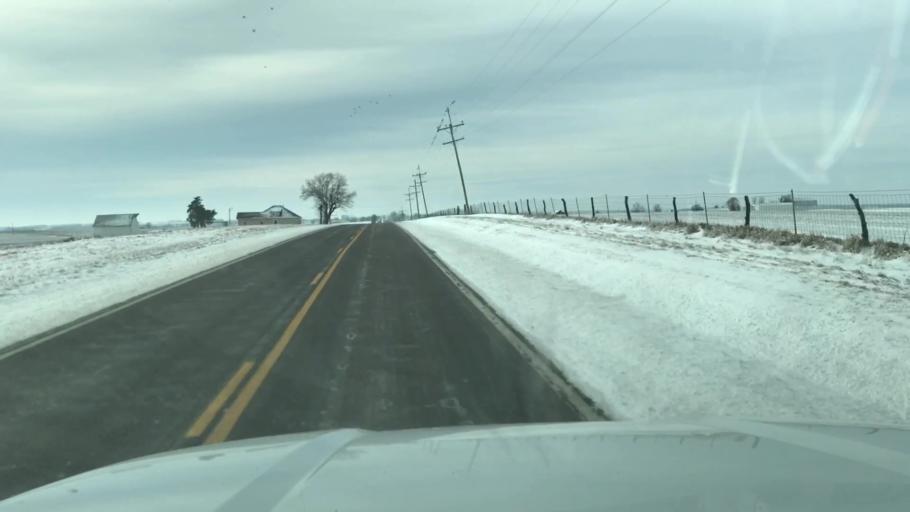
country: US
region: Missouri
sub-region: Holt County
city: Oregon
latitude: 40.0852
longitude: -95.1355
